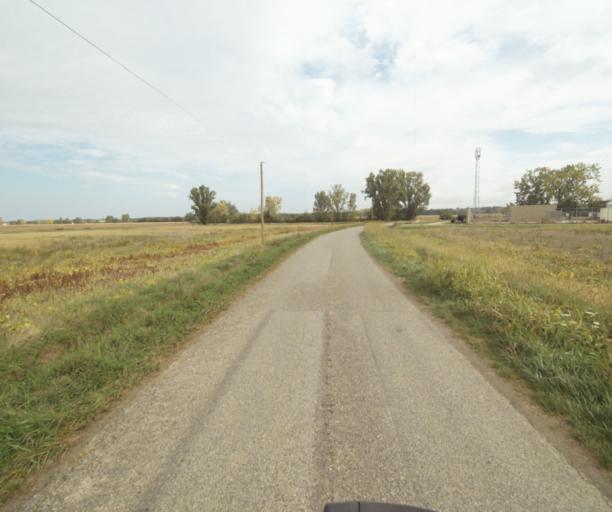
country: FR
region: Midi-Pyrenees
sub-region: Departement du Tarn-et-Garonne
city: Finhan
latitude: 43.9074
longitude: 1.2421
